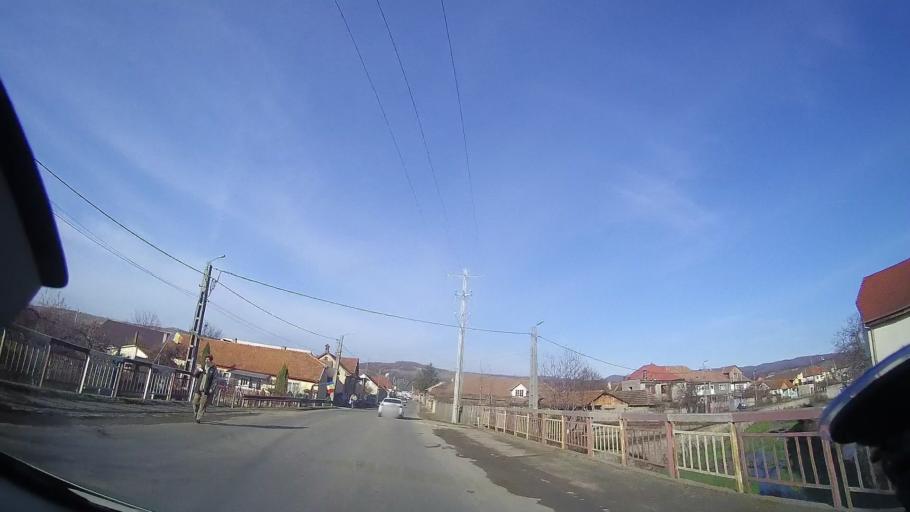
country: RO
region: Bihor
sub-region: Comuna Astileu
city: Astileu
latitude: 47.0557
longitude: 22.3914
